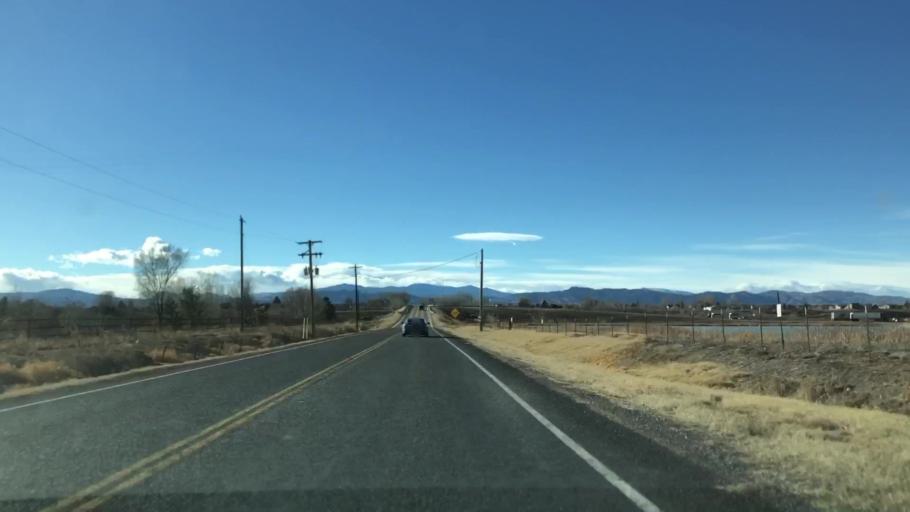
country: US
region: Colorado
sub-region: Weld County
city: Windsor
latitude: 40.5085
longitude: -104.9868
